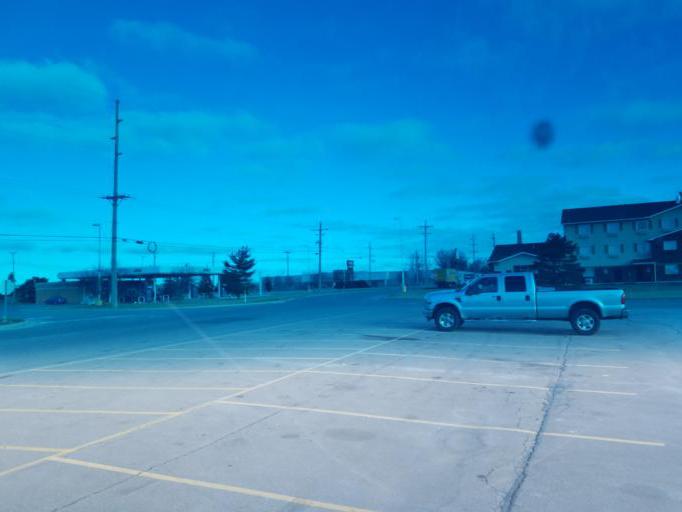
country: US
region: Ohio
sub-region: Marion County
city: Marion
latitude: 40.5800
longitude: -83.0733
